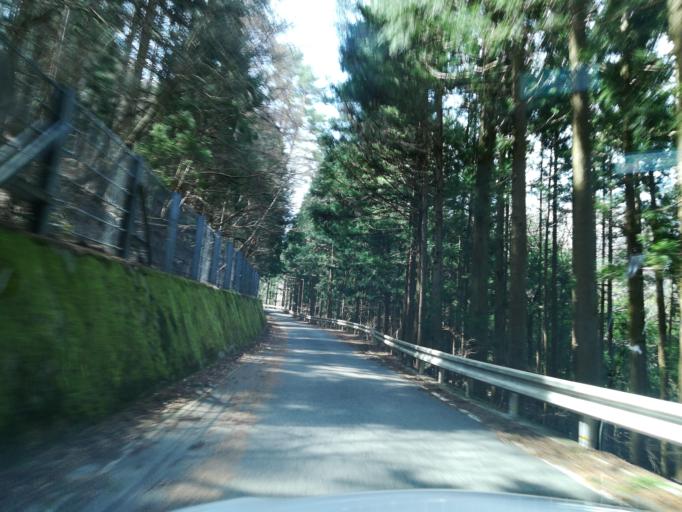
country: JP
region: Tokushima
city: Wakimachi
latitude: 33.8910
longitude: 134.0657
